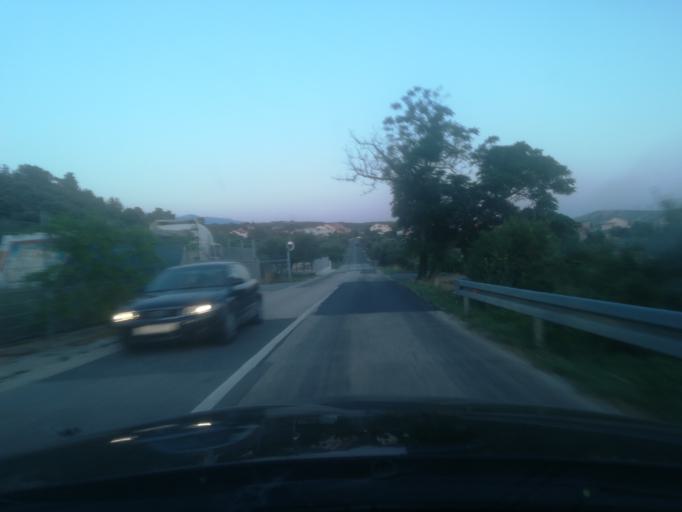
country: HR
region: Primorsko-Goranska
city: Banjol
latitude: 44.7342
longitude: 14.8084
